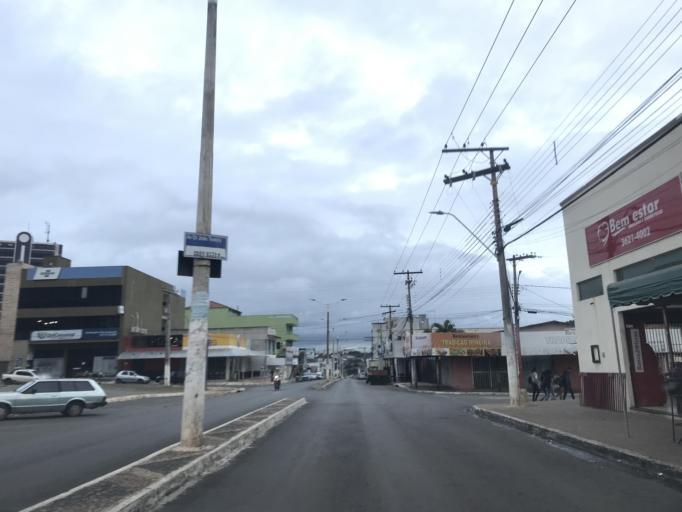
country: BR
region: Goias
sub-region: Luziania
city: Luziania
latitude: -16.2534
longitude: -47.9574
